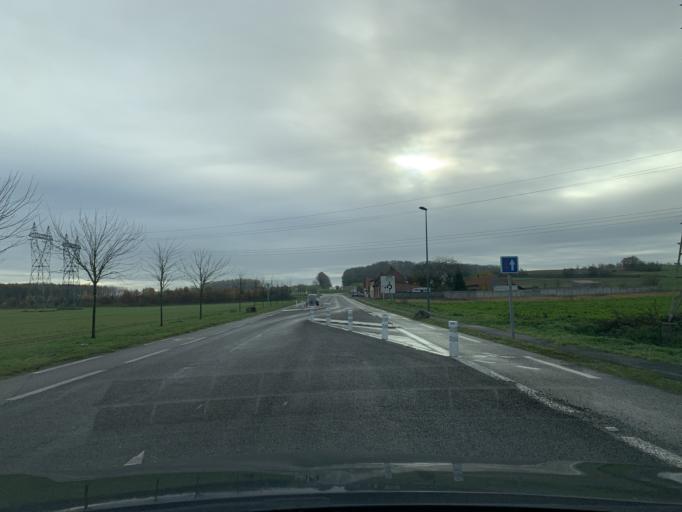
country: FR
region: Nord-Pas-de-Calais
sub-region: Departement du Nord
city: Cantin
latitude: 50.3071
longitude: 3.1306
